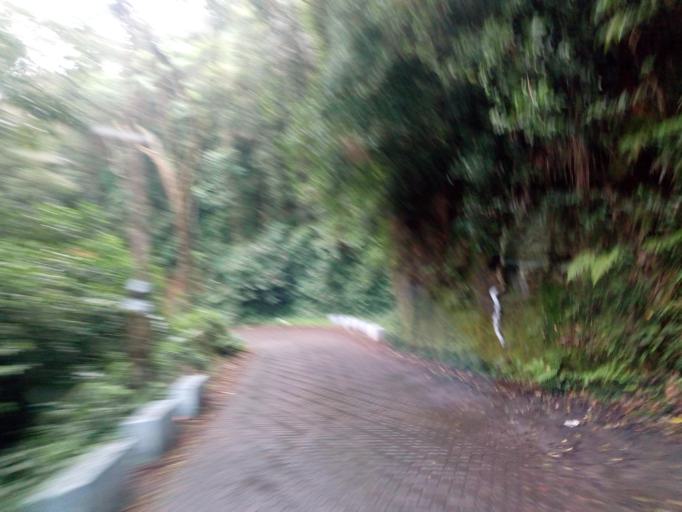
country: IN
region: Tamil Nadu
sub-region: Nilgiri
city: Wellington
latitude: 11.3619
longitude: 76.8389
